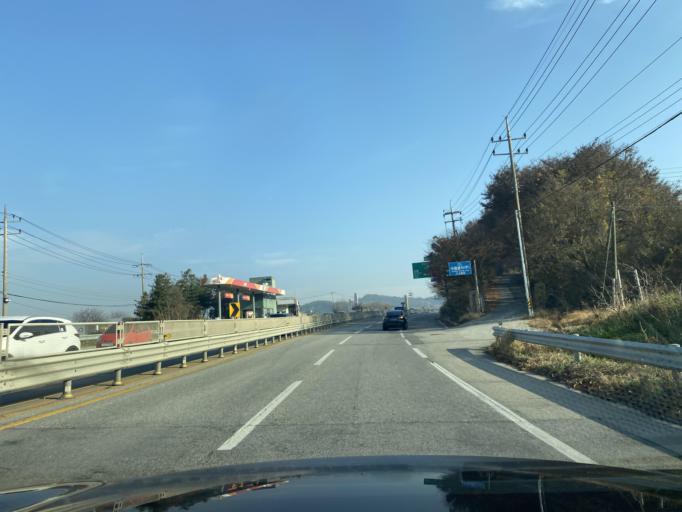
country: KR
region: Chungcheongnam-do
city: Yesan
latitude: 36.7440
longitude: 126.8613
